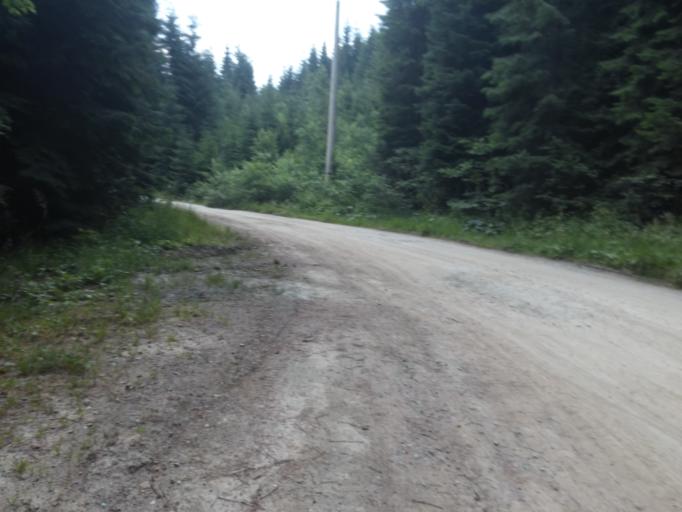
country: RO
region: Valcea
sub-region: Comuna Voineasa
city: Voineasa
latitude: 45.4306
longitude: 23.7558
